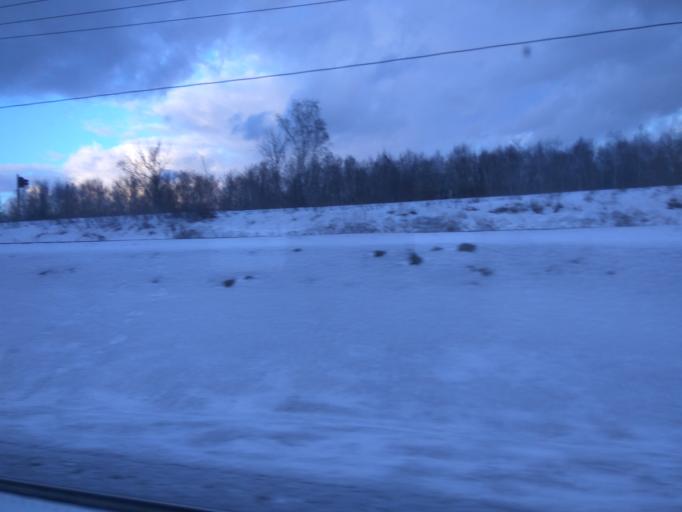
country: RU
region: Moscow
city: Tsaritsyno
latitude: 55.6160
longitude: 37.6341
